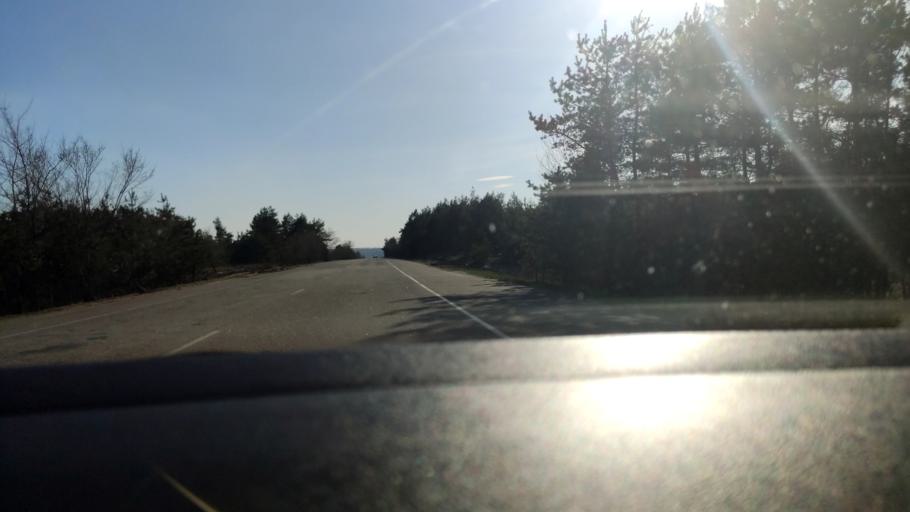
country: RU
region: Voronezj
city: Kolodeznyy
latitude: 51.3653
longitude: 39.1947
